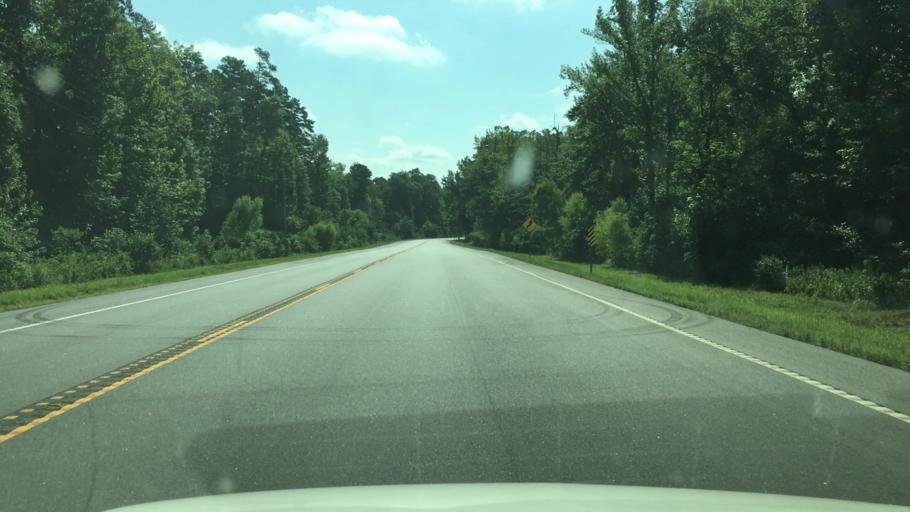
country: US
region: Arkansas
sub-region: Garland County
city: Rockwell
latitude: 34.5176
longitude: -93.3050
